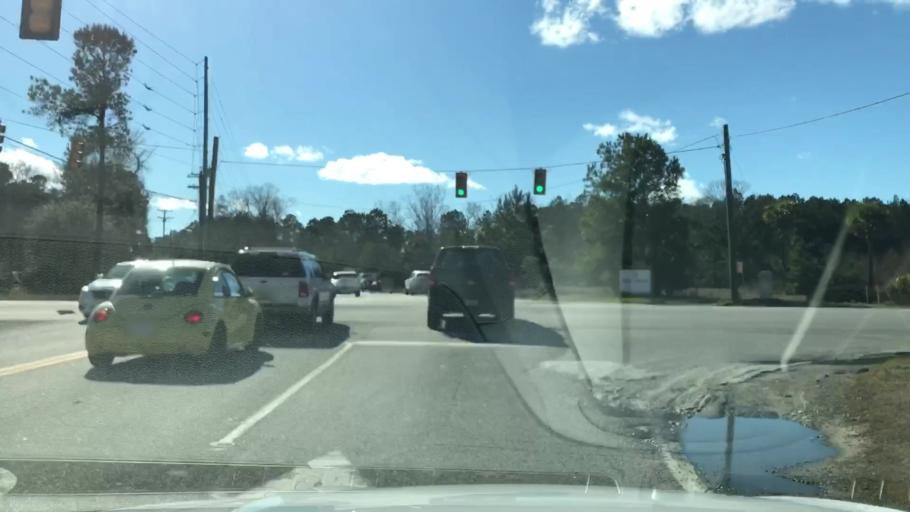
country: US
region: South Carolina
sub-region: Dorchester County
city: Summerville
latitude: 33.0559
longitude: -80.2382
